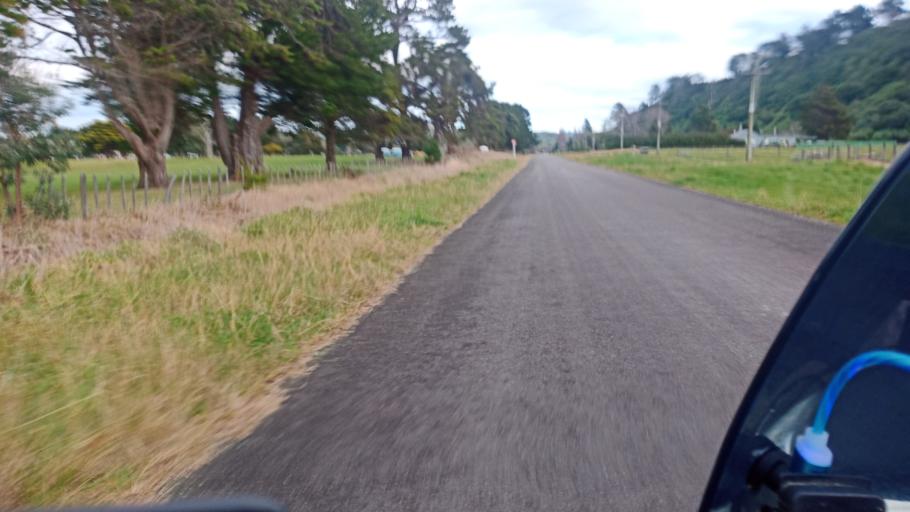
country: NZ
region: Gisborne
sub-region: Gisborne District
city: Gisborne
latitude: -38.3668
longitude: 178.3021
